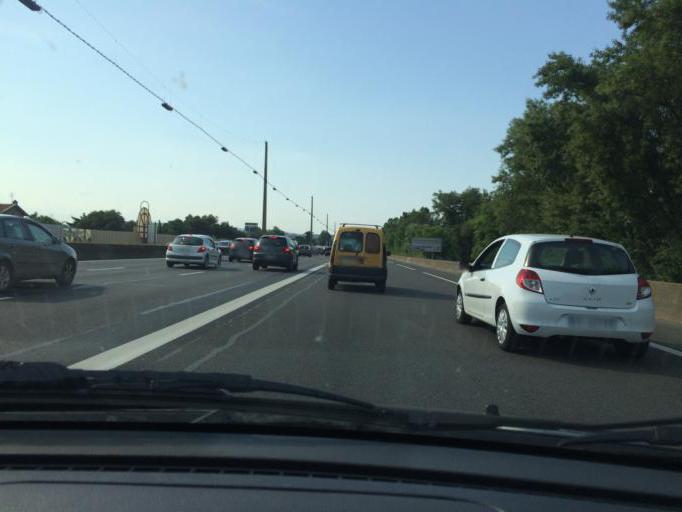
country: FR
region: Rhone-Alpes
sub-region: Departement du Rhone
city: Villeurbanne
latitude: 45.7703
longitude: 4.9027
